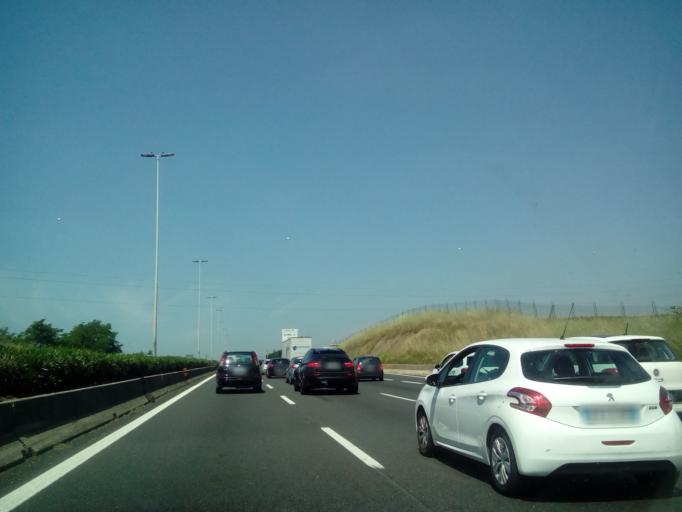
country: IT
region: Latium
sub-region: Citta metropolitana di Roma Capitale
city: Selcetta
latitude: 41.8003
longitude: 12.4590
